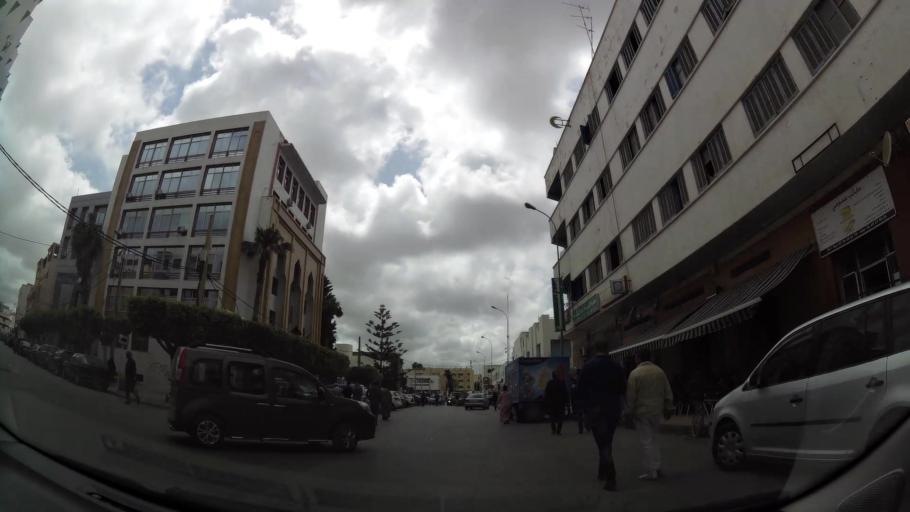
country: MA
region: Oriental
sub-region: Nador
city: Nador
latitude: 35.1762
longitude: -2.9240
